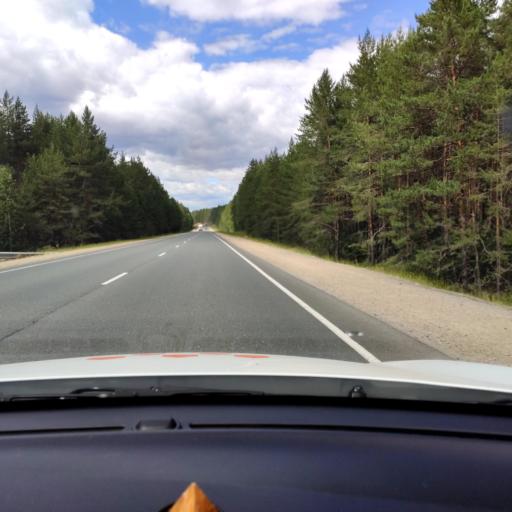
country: RU
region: Mariy-El
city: Pomary
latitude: 56.0538
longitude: 48.3735
